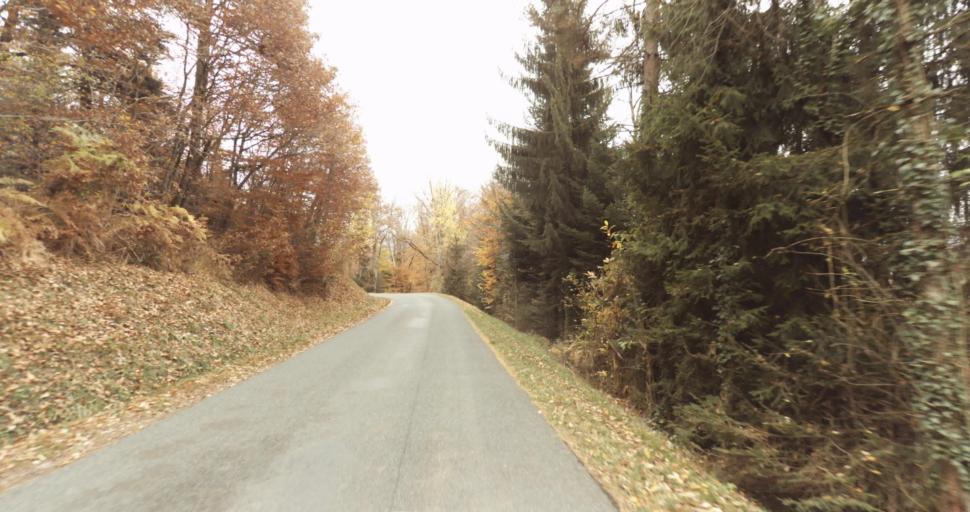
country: FR
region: Rhone-Alpes
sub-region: Departement de la Haute-Savoie
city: Saint-Martin-Bellevue
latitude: 45.9522
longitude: 6.1479
